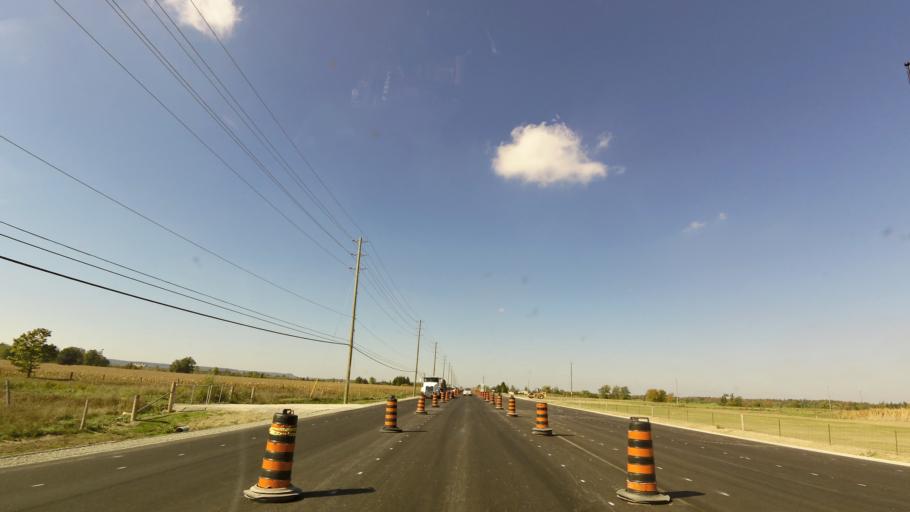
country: CA
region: Ontario
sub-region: Halton
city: Milton
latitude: 43.4718
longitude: -79.8141
